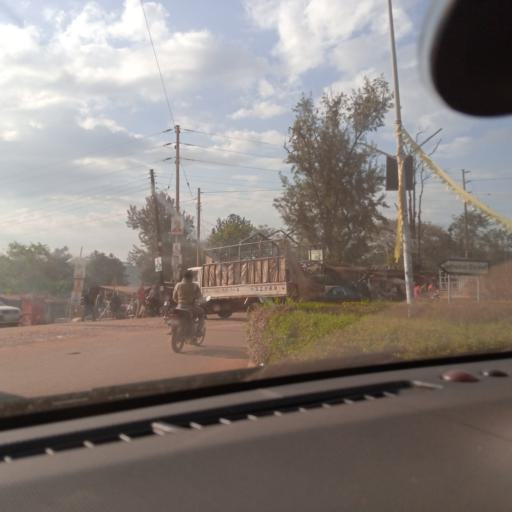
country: UG
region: Central Region
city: Masaka
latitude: -0.3479
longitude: 31.7390
